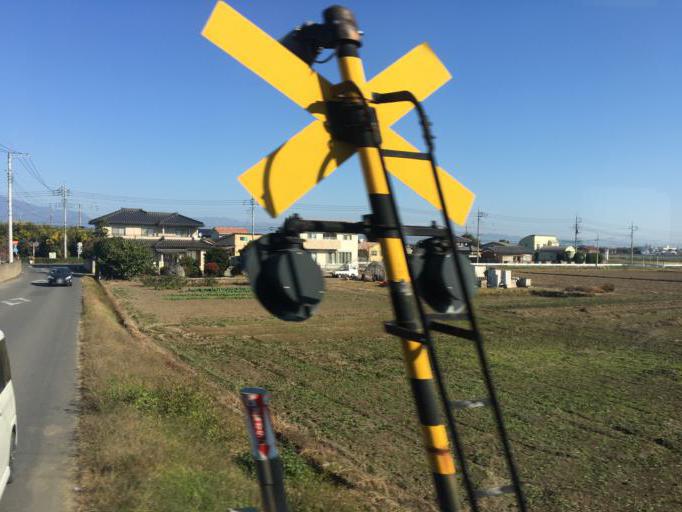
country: JP
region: Gunma
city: Isesaki
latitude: 36.3382
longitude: 139.1707
